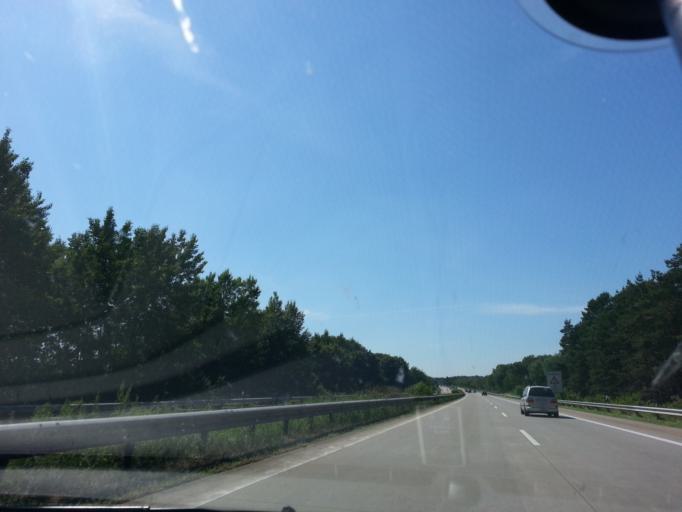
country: DE
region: Schleswig-Holstein
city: Guster
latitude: 53.5500
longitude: 10.6859
